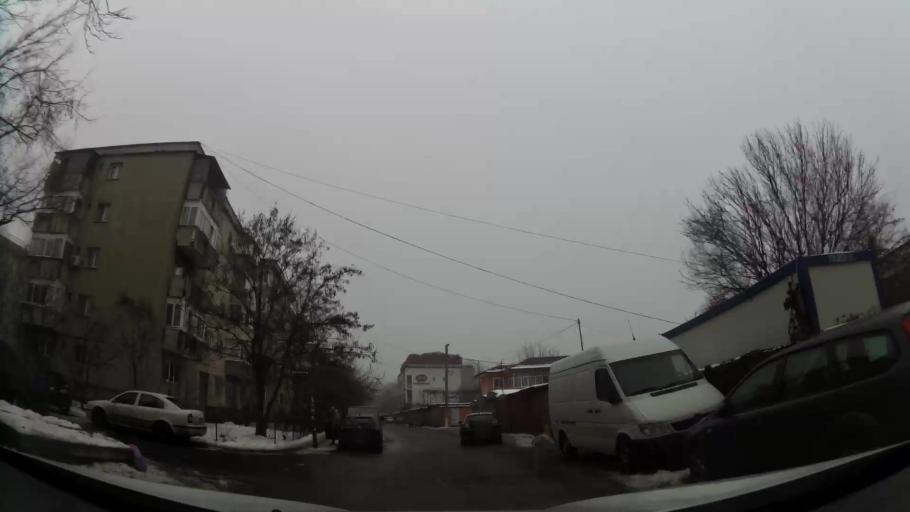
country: RO
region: Ilfov
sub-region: Comuna Chiajna
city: Rosu
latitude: 44.4424
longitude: 26.0172
